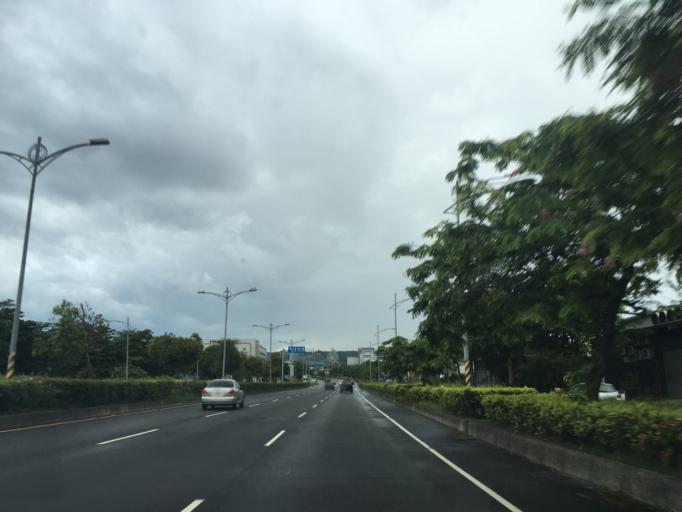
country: TW
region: Taiwan
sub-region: Taichung City
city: Taichung
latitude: 24.2054
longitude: 120.6313
